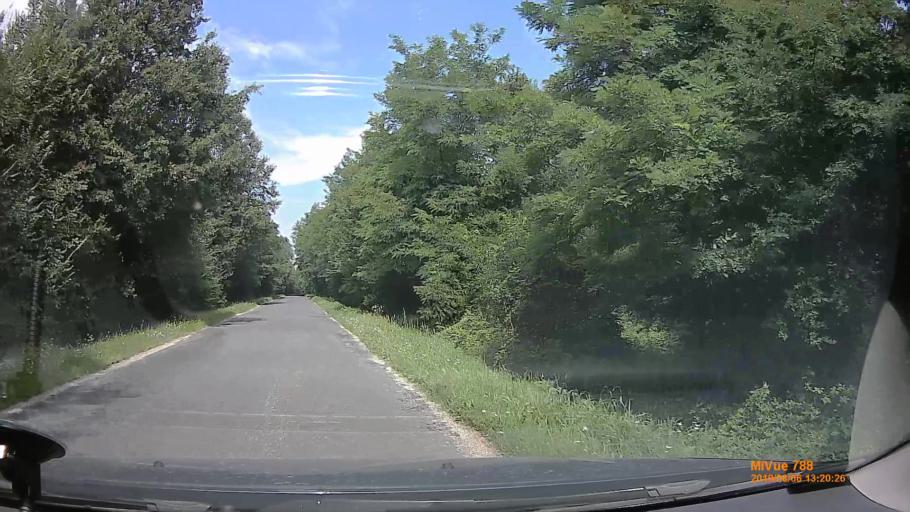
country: HU
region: Zala
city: Pacsa
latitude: 46.6381
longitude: 17.0759
